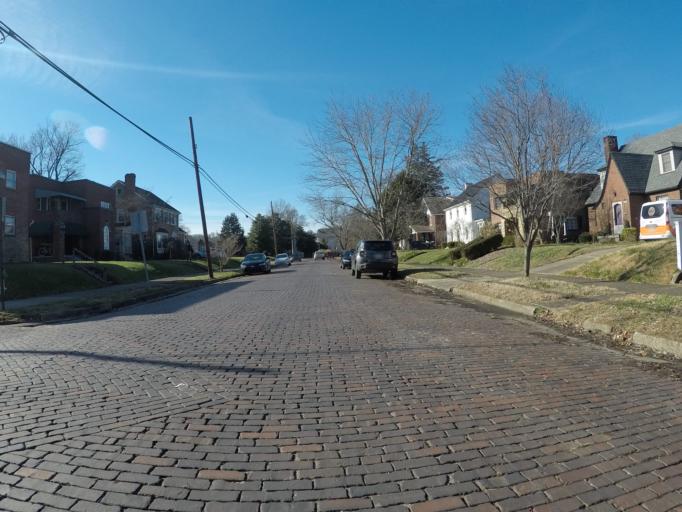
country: US
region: West Virginia
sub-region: Cabell County
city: Huntington
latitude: 38.4105
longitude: -82.4342
